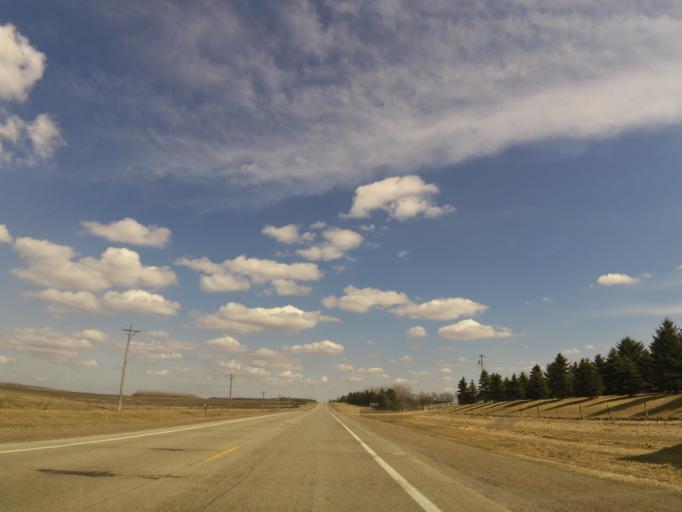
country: US
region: South Dakota
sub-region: Codington County
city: Watertown
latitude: 44.8901
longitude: -96.9596
